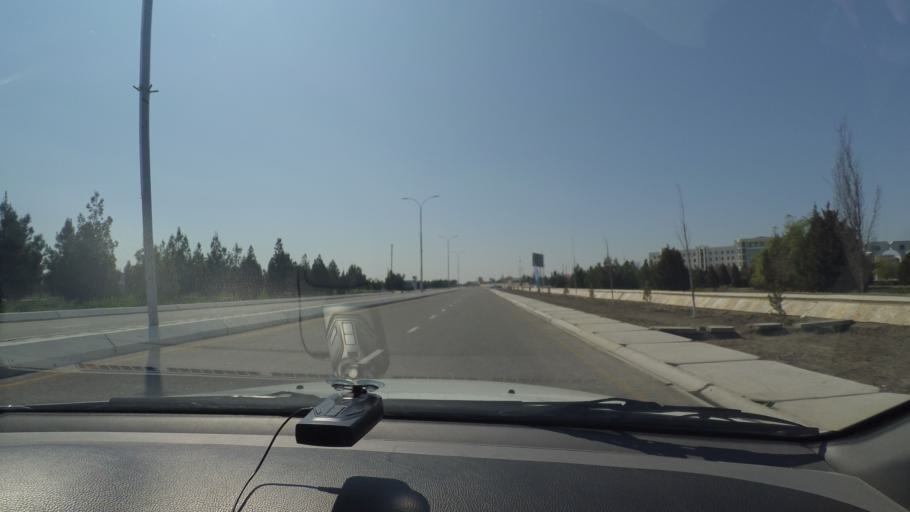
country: UZ
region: Bukhara
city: Bukhara
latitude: 39.7684
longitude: 64.4730
